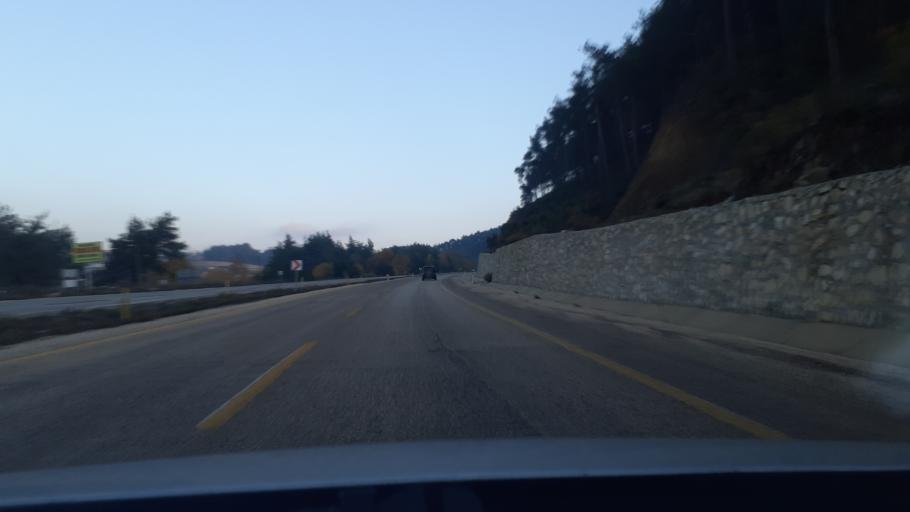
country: TR
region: Hatay
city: Yayladagi
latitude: 35.8946
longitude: 36.0818
